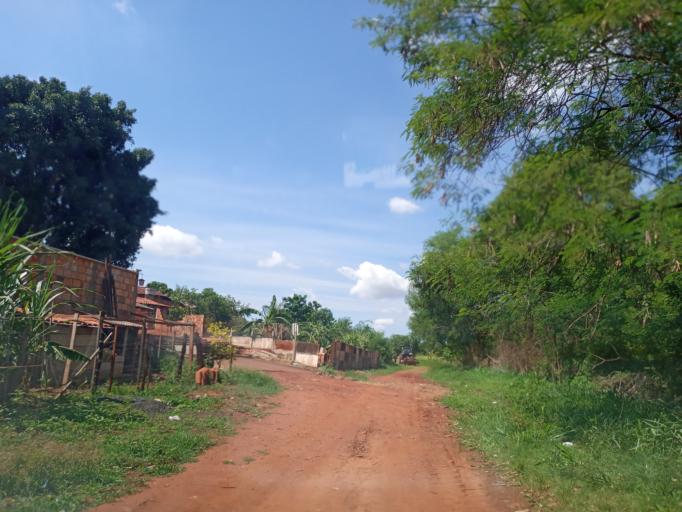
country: BR
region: Minas Gerais
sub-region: Ituiutaba
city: Ituiutaba
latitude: -18.9954
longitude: -49.4764
